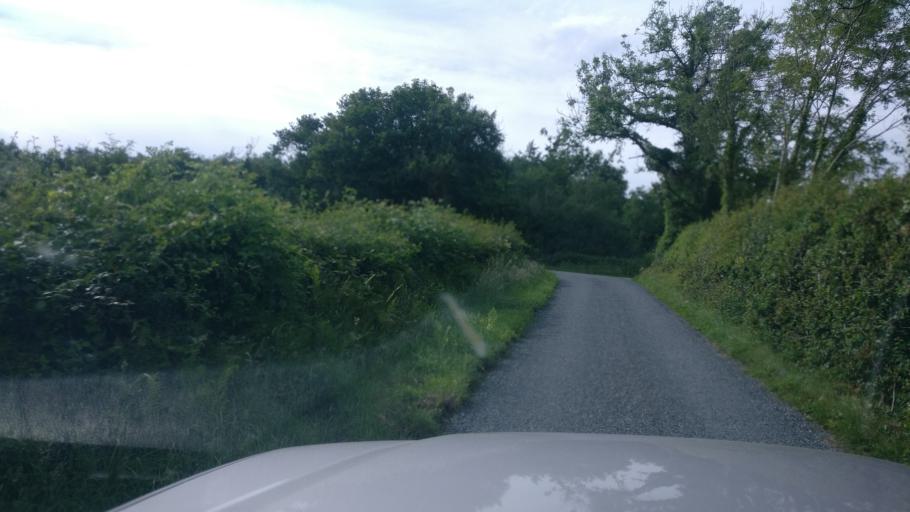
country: IE
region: Connaught
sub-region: County Galway
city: Gort
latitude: 53.1104
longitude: -8.7183
